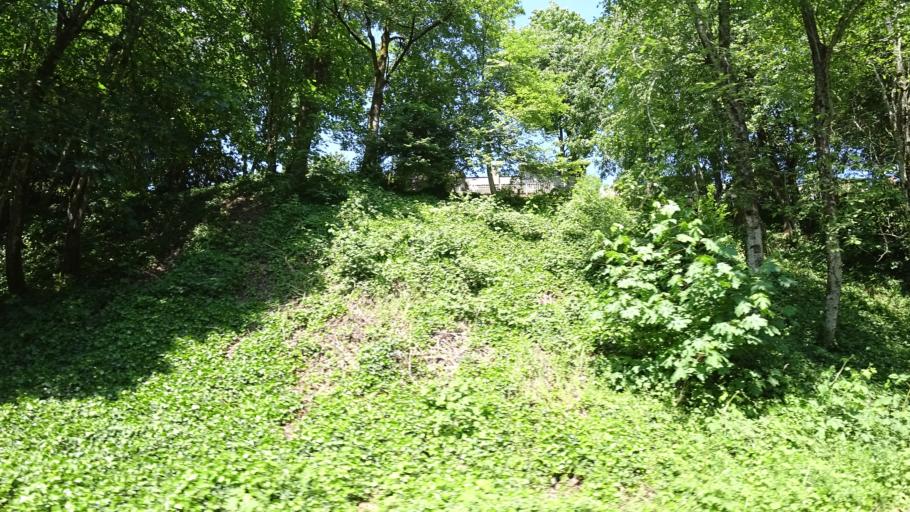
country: US
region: Oregon
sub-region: Clackamas County
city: Lake Oswego
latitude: 45.4292
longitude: -122.7081
